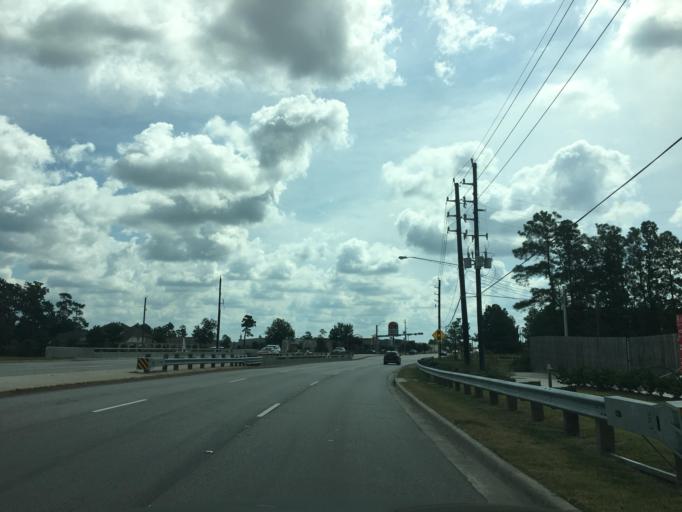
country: US
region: Texas
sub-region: Harris County
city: Spring
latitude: 30.1229
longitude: -95.4039
